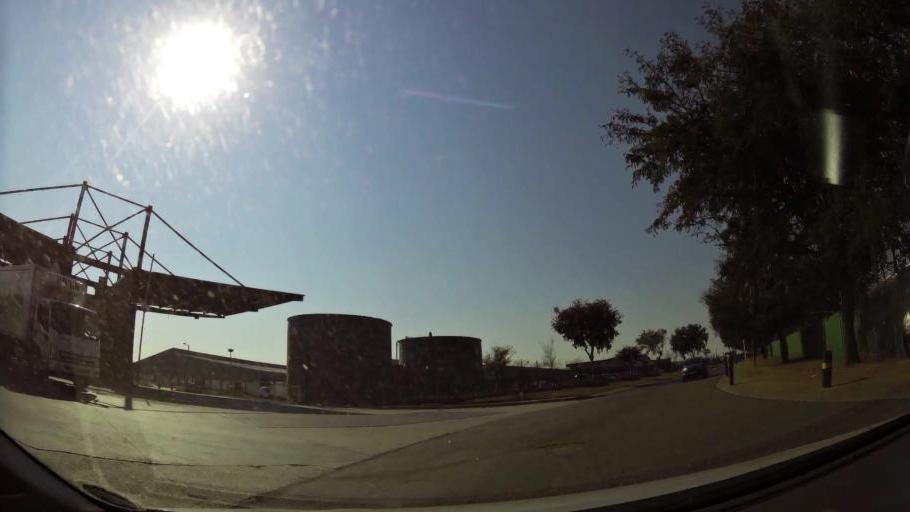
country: ZA
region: Gauteng
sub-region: City of Johannesburg Metropolitan Municipality
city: Modderfontein
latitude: -26.1079
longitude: 28.1331
